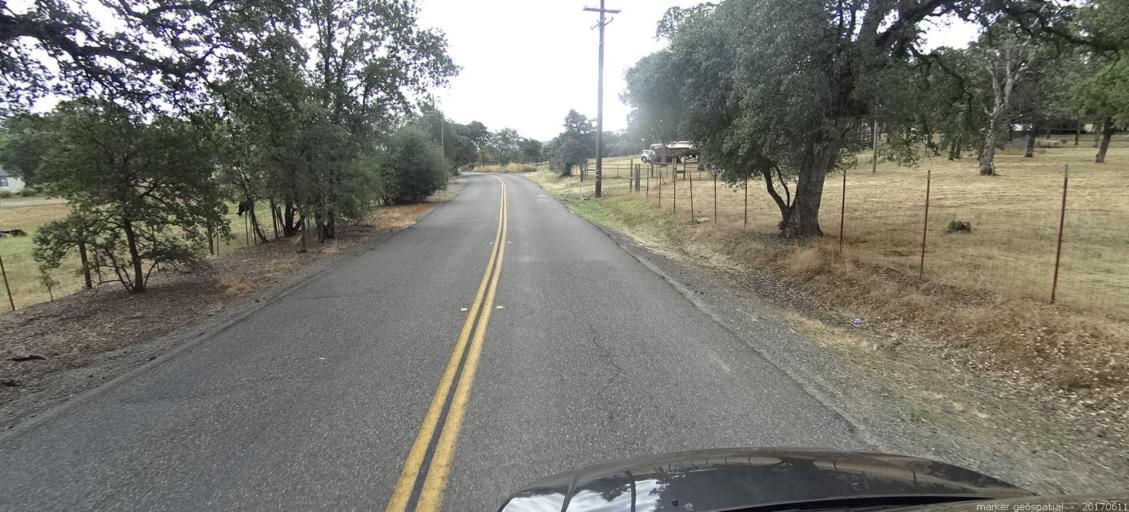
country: US
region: California
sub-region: Yuba County
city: Loma Rica
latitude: 39.3818
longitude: -121.3950
